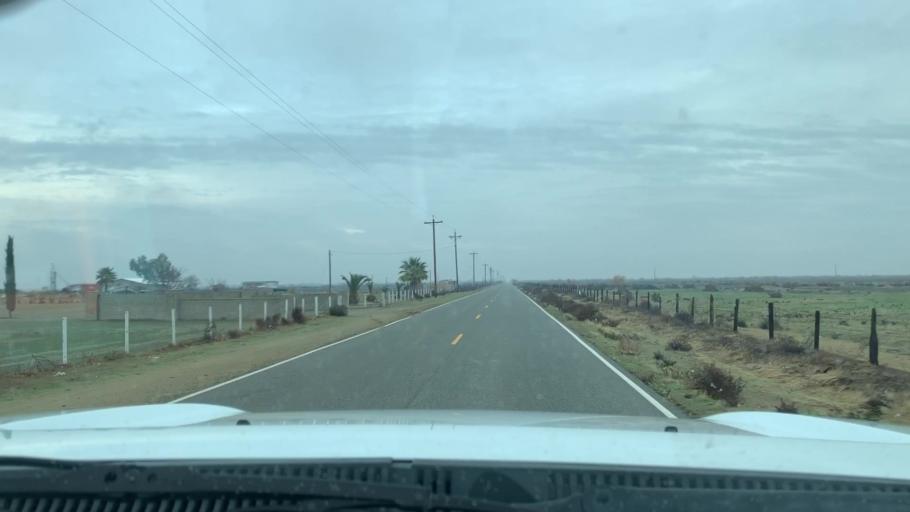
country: US
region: California
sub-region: Kern County
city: Lost Hills
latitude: 35.6979
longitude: -119.5797
